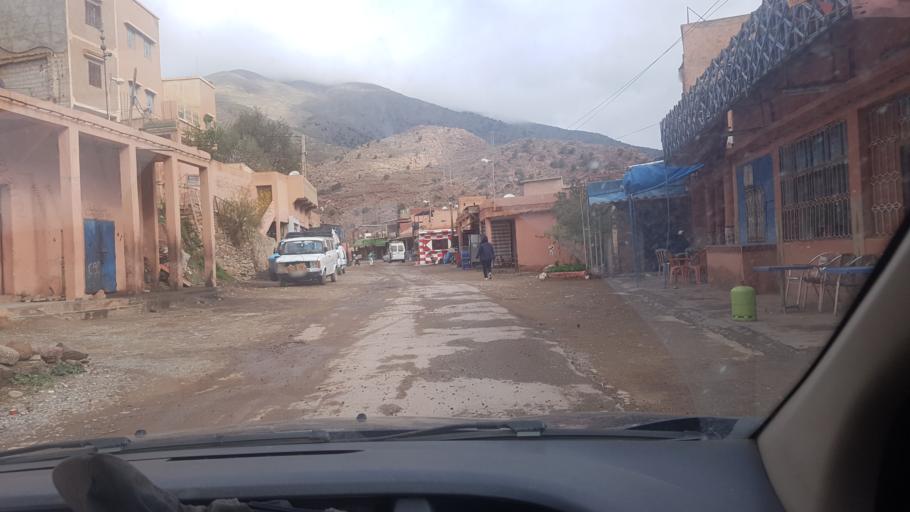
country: MA
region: Marrakech-Tensift-Al Haouz
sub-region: Al-Haouz
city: Azgour
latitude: 30.9988
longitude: -8.1580
